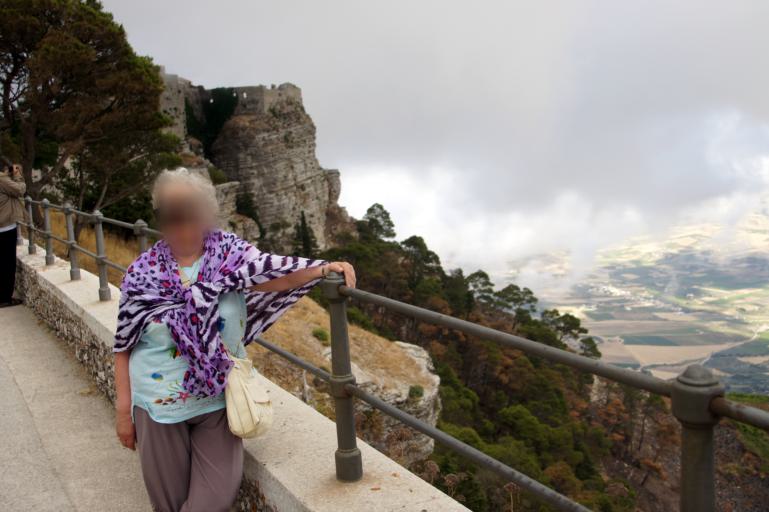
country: IT
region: Sicily
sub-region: Trapani
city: Erice
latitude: 38.0357
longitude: 12.5886
